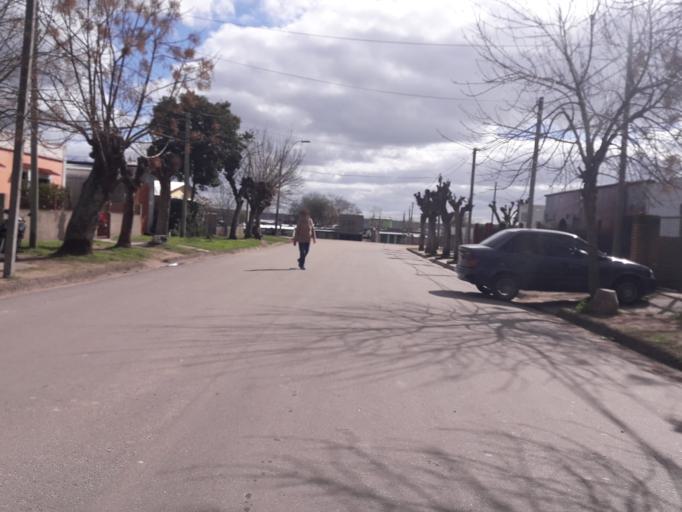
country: UY
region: Durazno
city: Santa Bernardina
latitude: -33.3700
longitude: -56.5304
